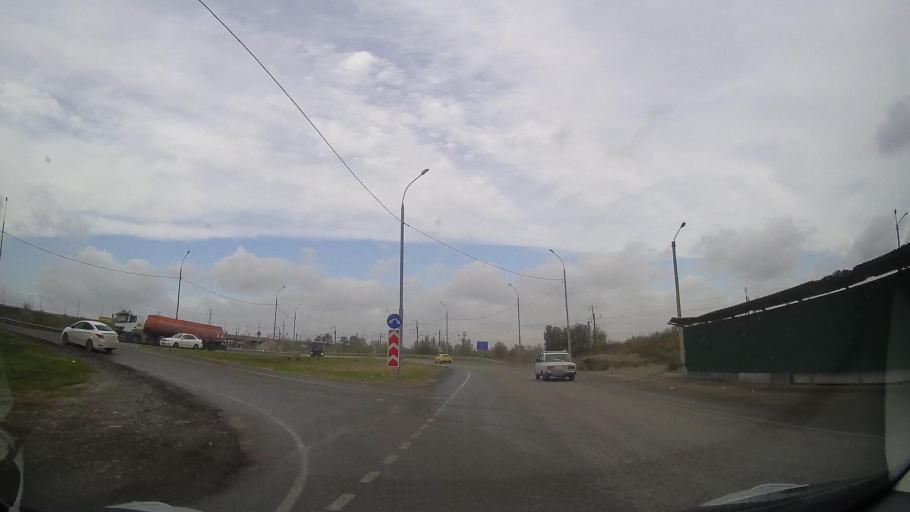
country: RU
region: Rostov
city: Bataysk
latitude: 47.1584
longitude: 39.7445
